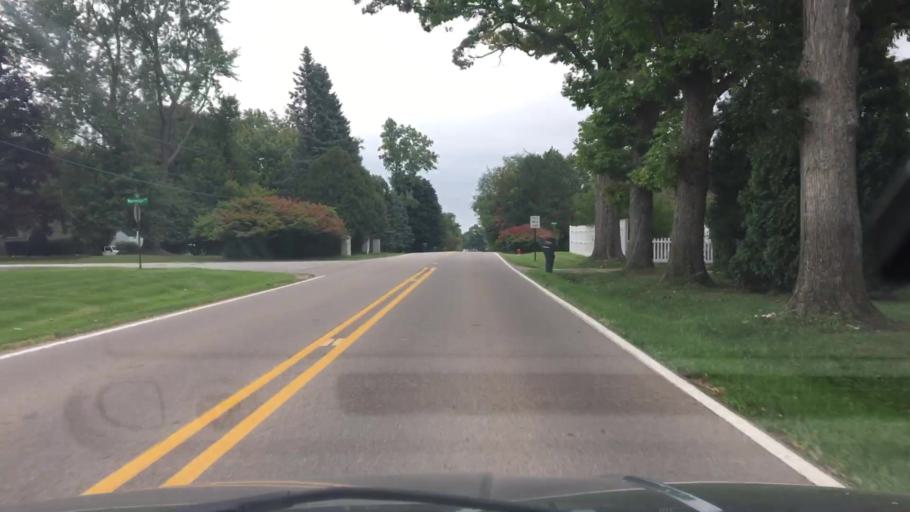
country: US
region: Michigan
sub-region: Livingston County
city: Brighton
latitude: 42.5074
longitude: -83.7783
